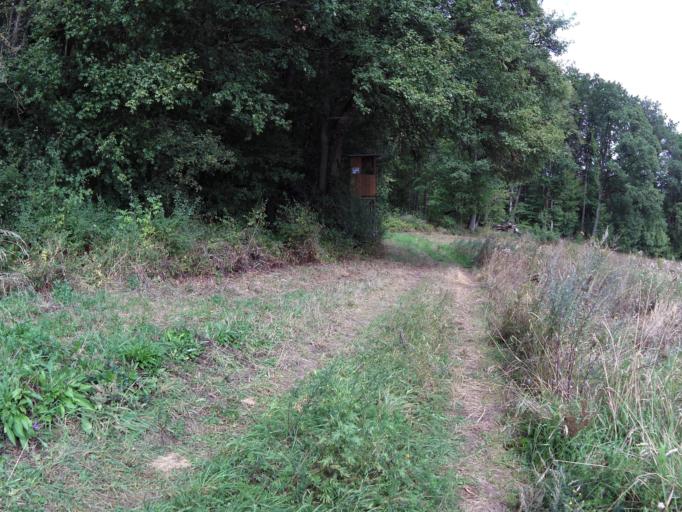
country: DE
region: Bavaria
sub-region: Regierungsbezirk Unterfranken
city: Kleinrinderfeld
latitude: 49.7114
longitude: 9.8281
